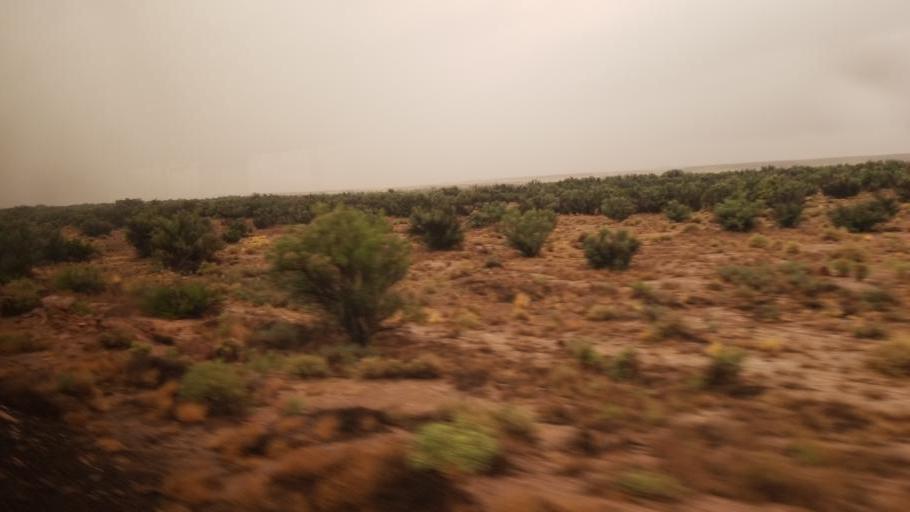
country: US
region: Arizona
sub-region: Navajo County
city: Joseph City
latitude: 34.9568
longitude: -110.3671
